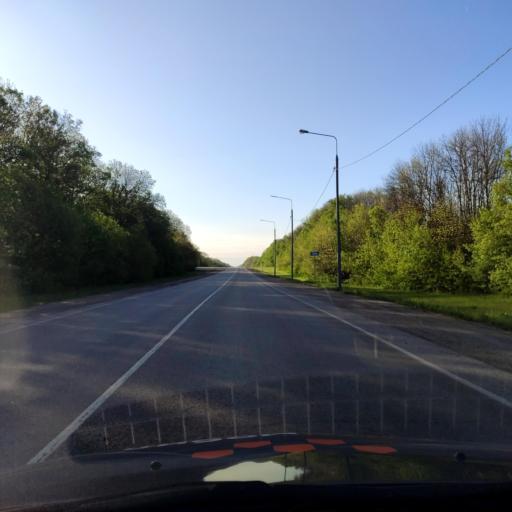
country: RU
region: Lipetsk
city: Yelets
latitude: 52.5797
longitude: 38.6375
